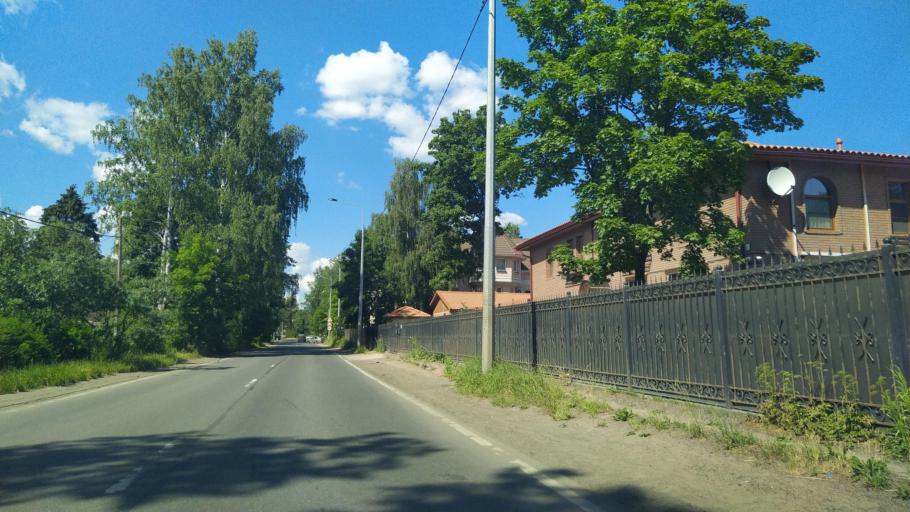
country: RU
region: St.-Petersburg
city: Ozerki
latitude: 60.0320
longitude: 30.3136
